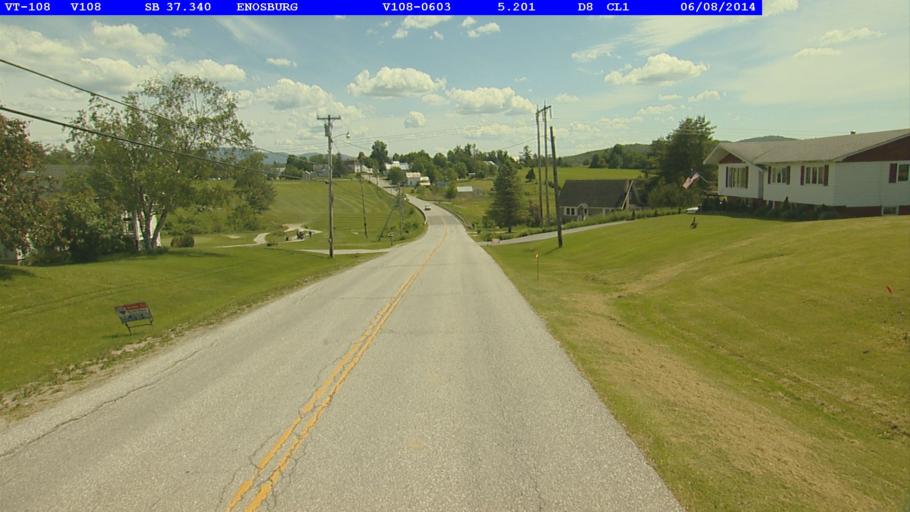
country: US
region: Vermont
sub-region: Franklin County
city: Enosburg Falls
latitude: 44.9153
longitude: -72.8052
